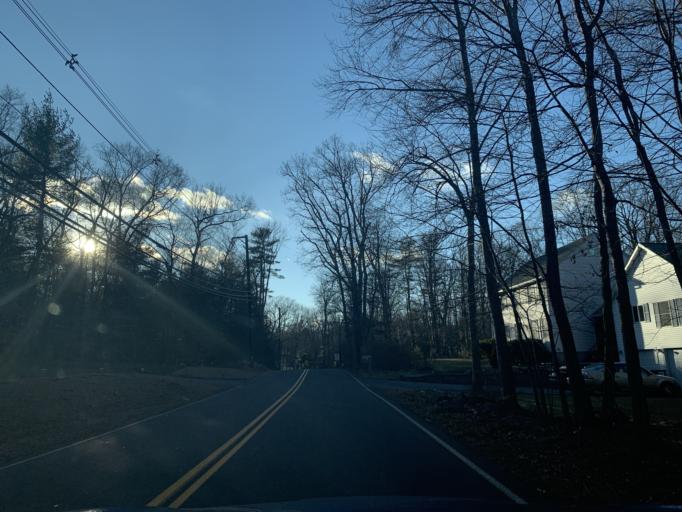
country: US
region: Massachusetts
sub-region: Bristol County
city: Norton
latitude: 41.9561
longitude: -71.1884
